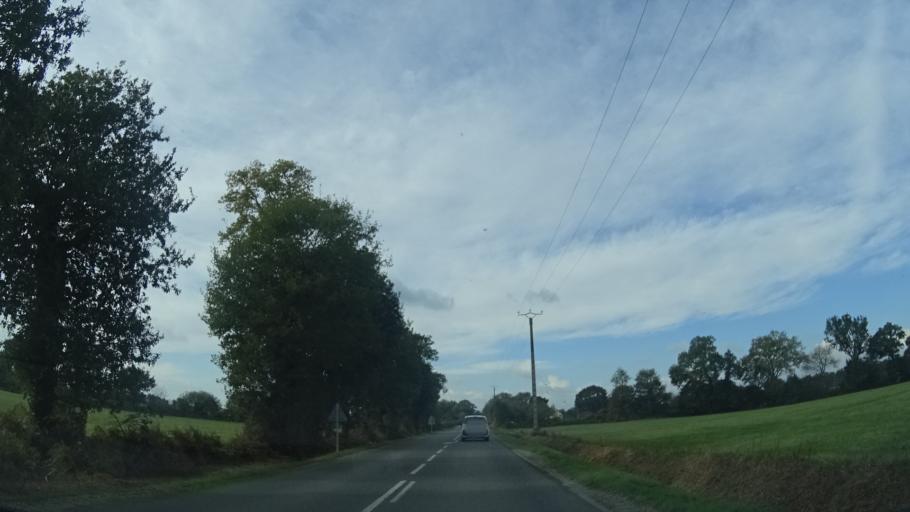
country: FR
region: Brittany
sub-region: Departement d'Ille-et-Vilaine
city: Meillac
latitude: 48.4321
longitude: -1.7911
